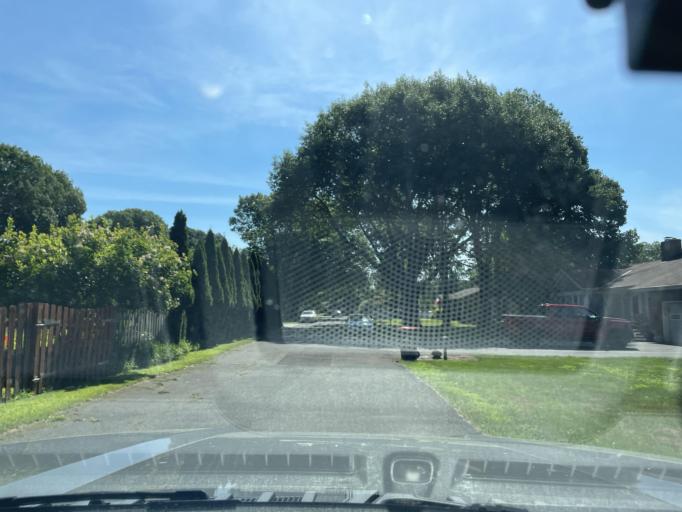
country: US
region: New York
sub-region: Ulster County
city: Saugerties South
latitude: 42.0624
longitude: -73.9581
